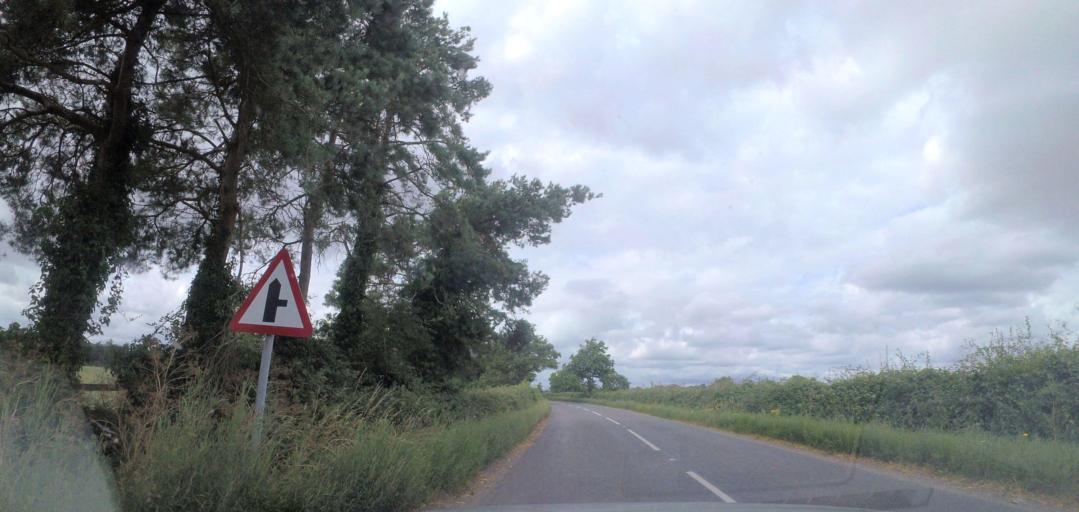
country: GB
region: England
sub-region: Suffolk
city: Bury St Edmunds
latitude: 52.2675
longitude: 0.5627
